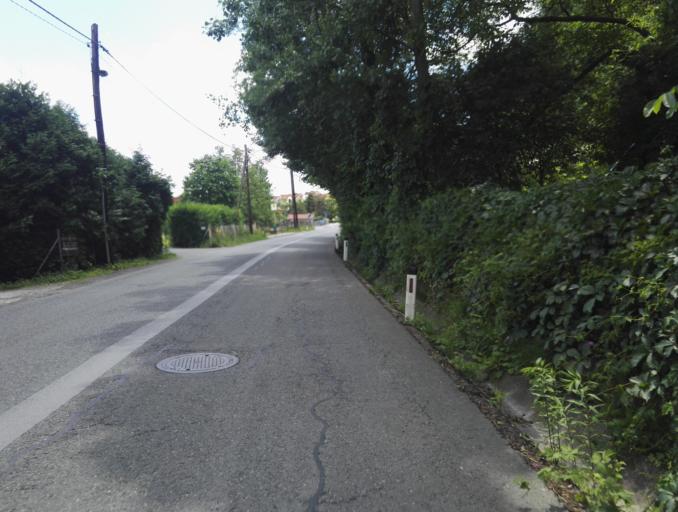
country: AT
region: Styria
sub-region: Graz Stadt
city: Goesting
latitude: 47.0852
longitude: 15.4031
